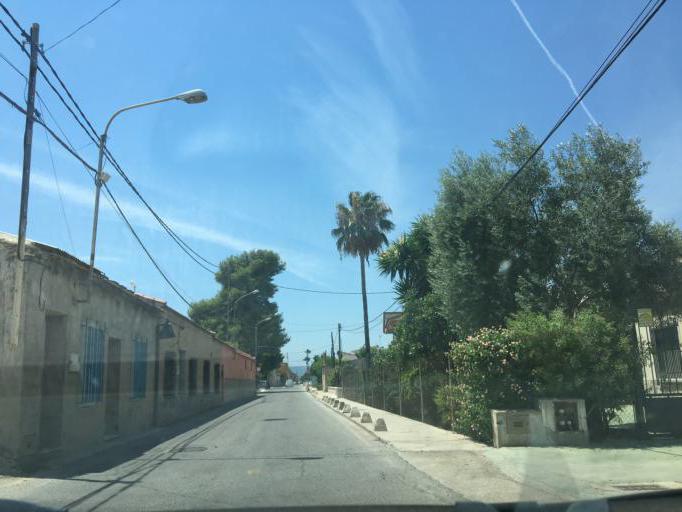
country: ES
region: Murcia
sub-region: Murcia
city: Santomera
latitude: 38.0318
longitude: -1.0629
